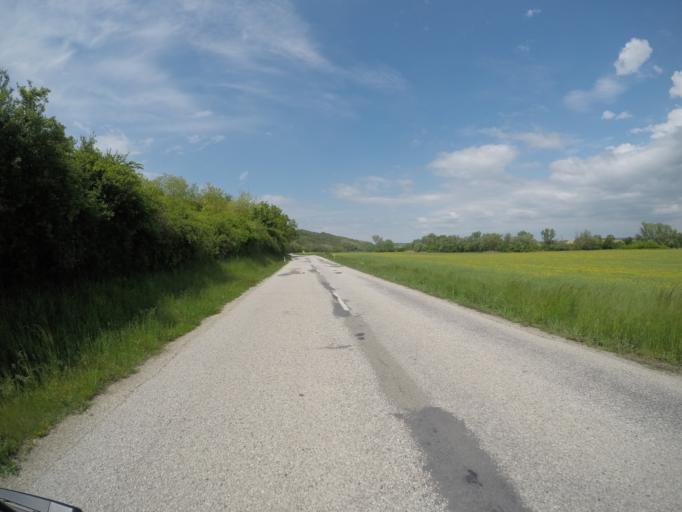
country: SK
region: Nitriansky
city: Zeliezovce
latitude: 47.9405
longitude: 18.7418
